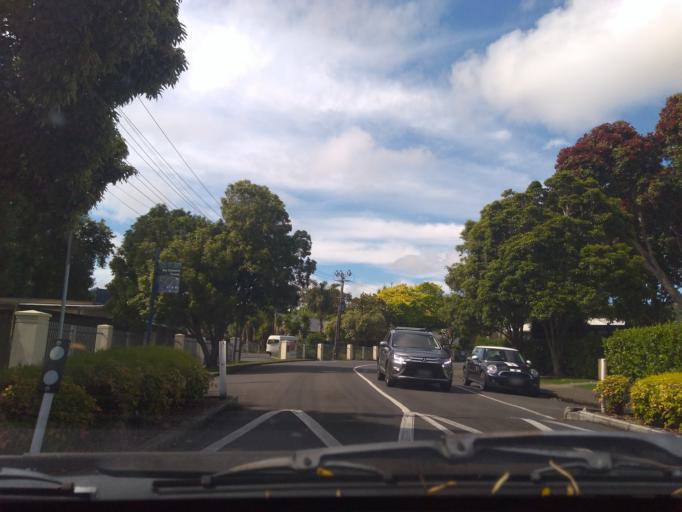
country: NZ
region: Auckland
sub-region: Auckland
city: Auckland
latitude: -36.8823
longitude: 174.7264
